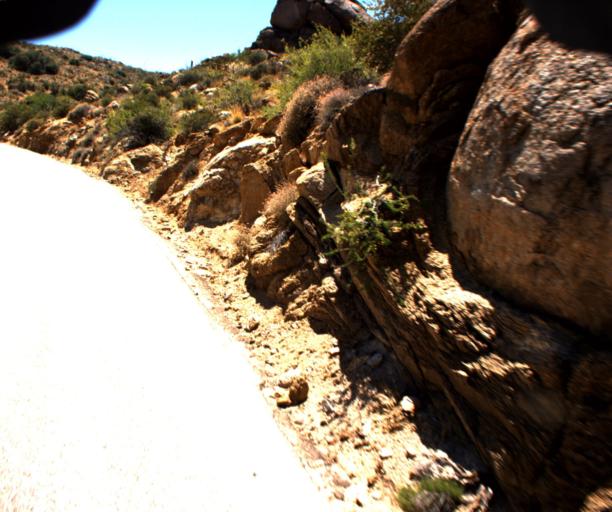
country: US
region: Arizona
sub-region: Yavapai County
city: Bagdad
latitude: 34.4516
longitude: -112.9764
